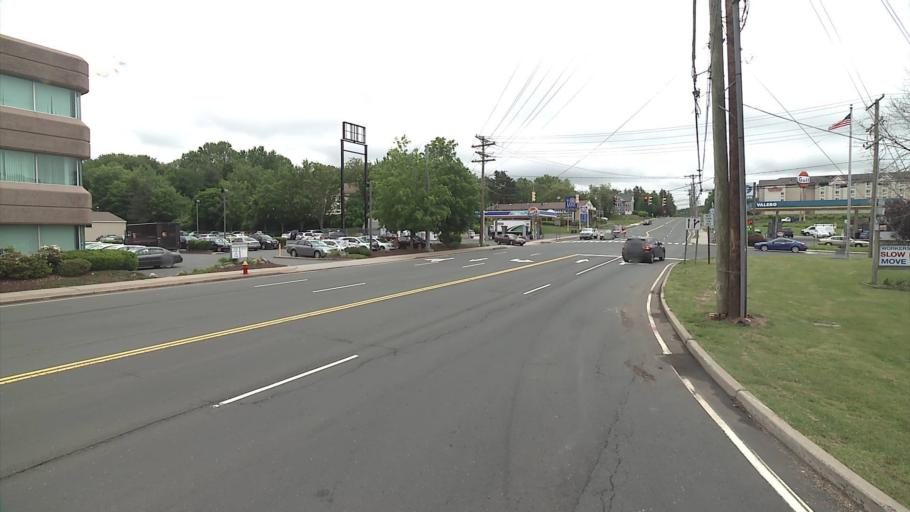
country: US
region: Connecticut
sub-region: New Haven County
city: Meriden
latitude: 41.5261
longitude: -72.7678
